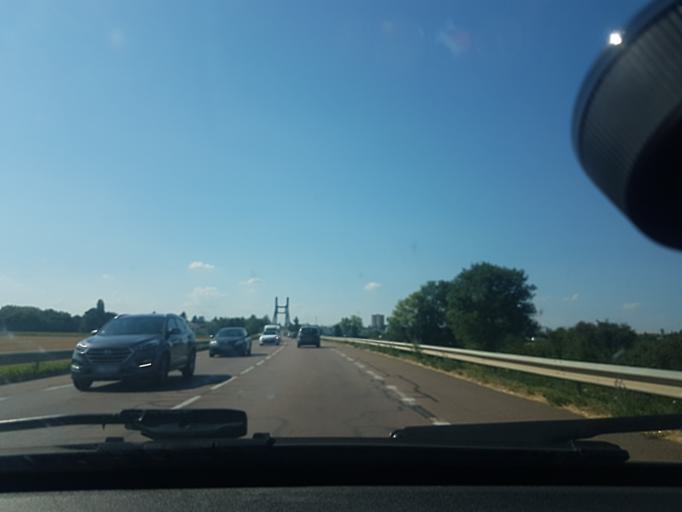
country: FR
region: Bourgogne
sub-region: Departement de Saone-et-Loire
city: Saint-Marcel
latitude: 46.7808
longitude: 4.8755
